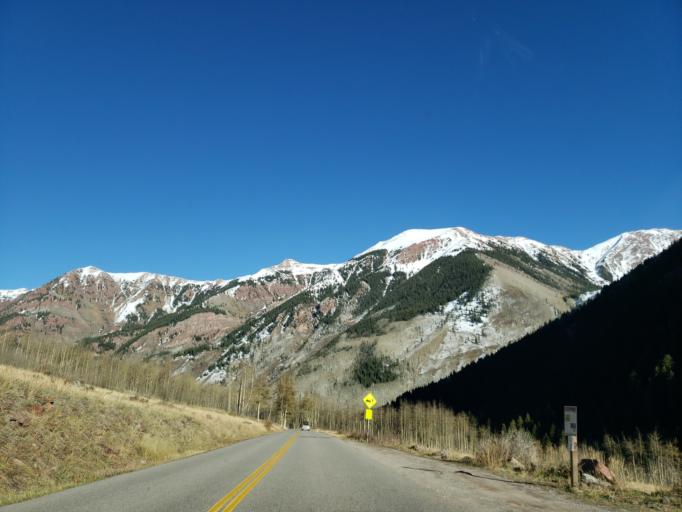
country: US
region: Colorado
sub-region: Pitkin County
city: Snowmass Village
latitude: 39.1049
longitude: -106.9294
